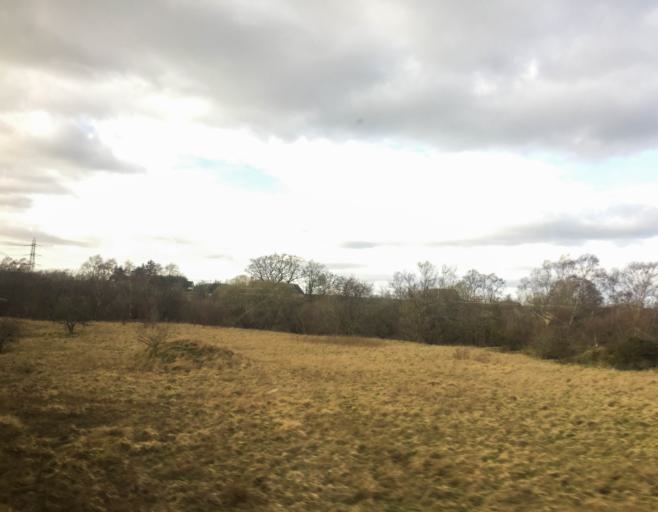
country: GB
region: Scotland
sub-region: North Lanarkshire
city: Newmains
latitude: 55.7586
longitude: -3.8860
